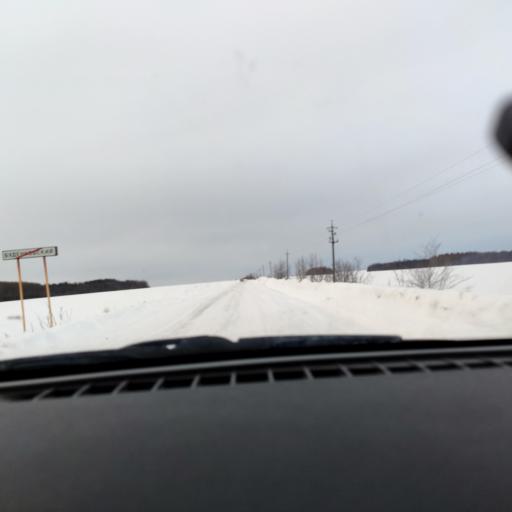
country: RU
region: Bashkortostan
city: Iglino
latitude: 54.7407
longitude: 56.5377
